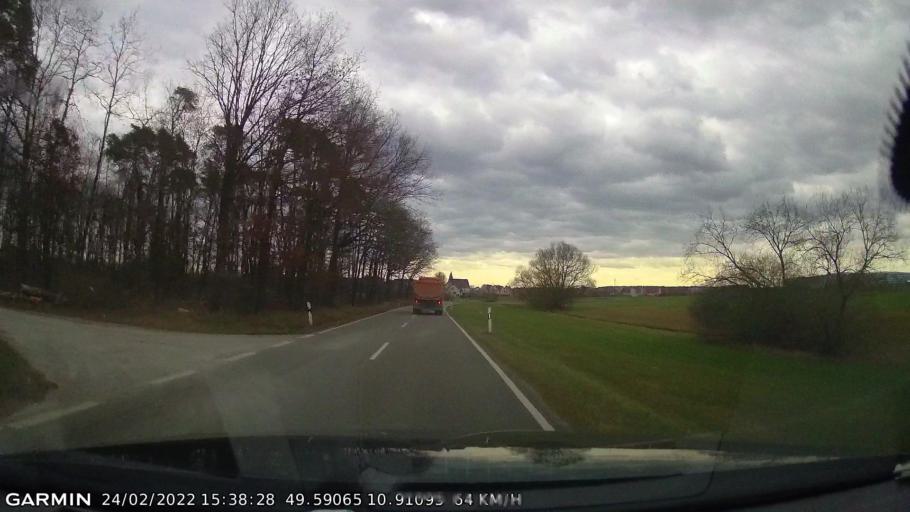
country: DE
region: Bavaria
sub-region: Regierungsbezirk Mittelfranken
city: Herzogenaurach
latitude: 49.5907
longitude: 10.9108
